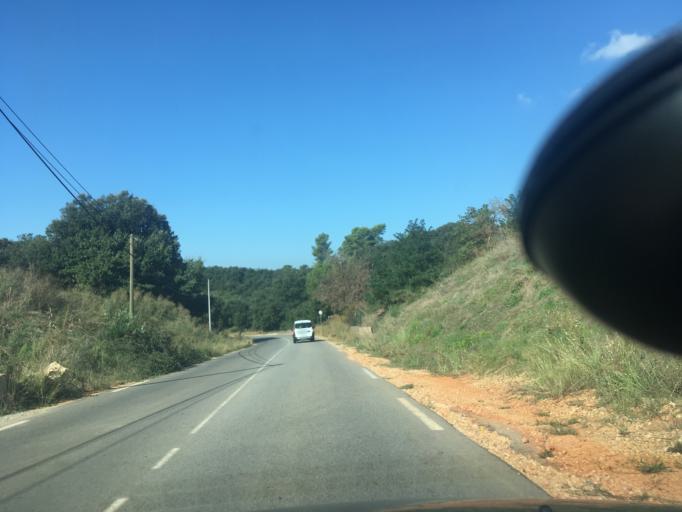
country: FR
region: Provence-Alpes-Cote d'Azur
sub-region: Departement du Var
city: Barjols
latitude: 43.5965
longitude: 6.0367
